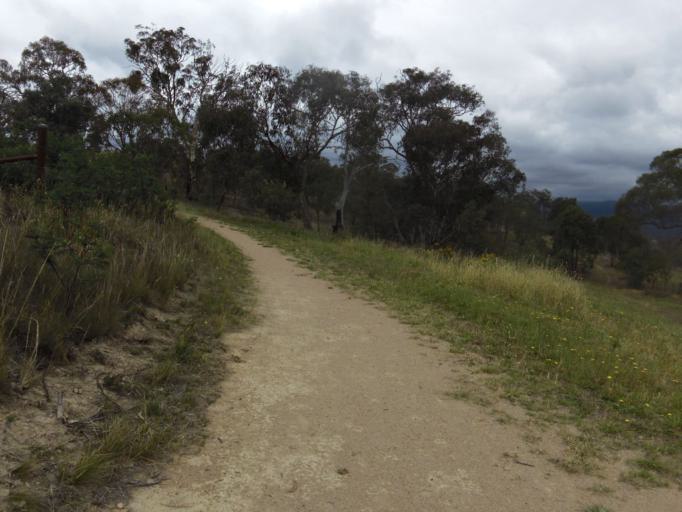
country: AU
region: Australian Capital Territory
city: Macquarie
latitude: -35.3509
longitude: 149.0210
